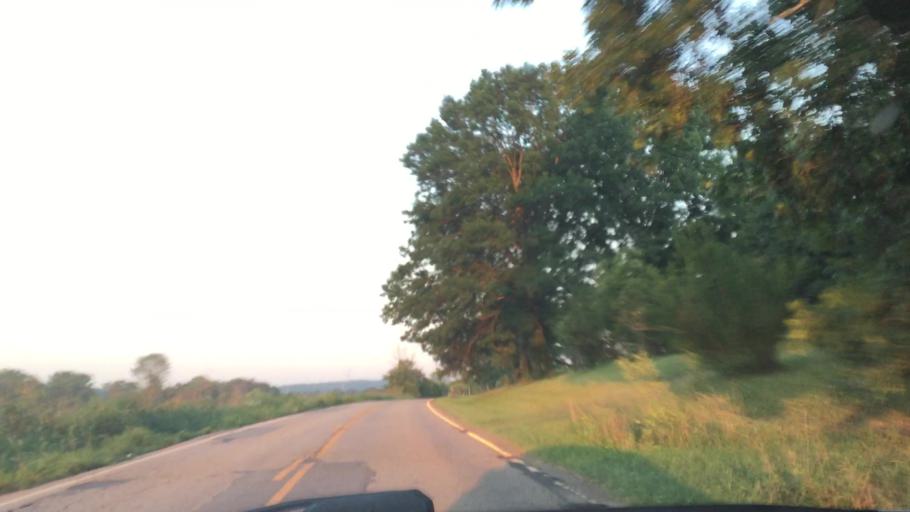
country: US
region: Kentucky
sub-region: Carroll County
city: Carrollton
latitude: 38.6458
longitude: -85.1535
